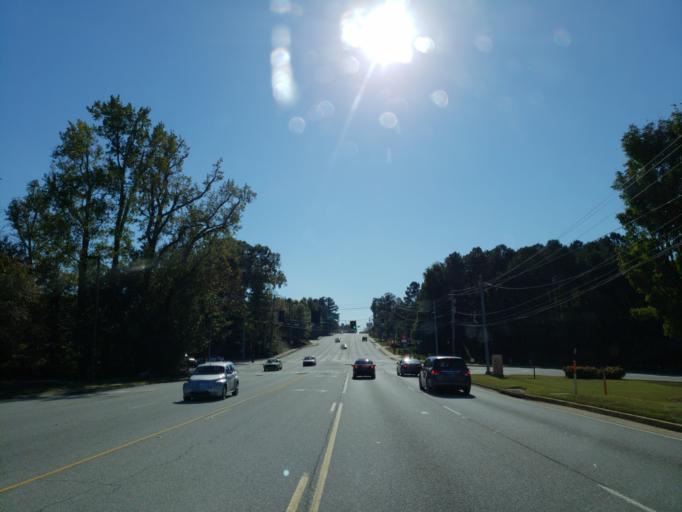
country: US
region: Georgia
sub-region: Gwinnett County
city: Lawrenceville
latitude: 33.9542
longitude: -83.9958
